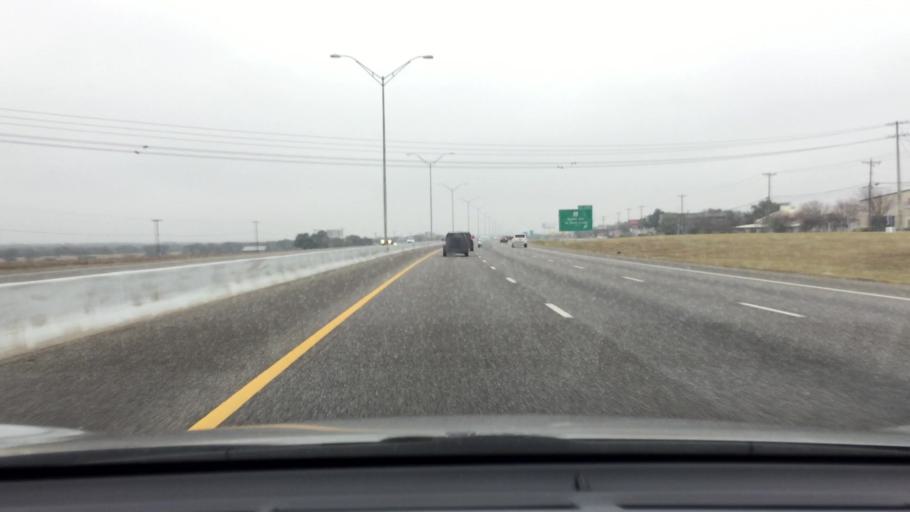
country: US
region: Texas
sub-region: Williamson County
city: Georgetown
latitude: 30.5938
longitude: -97.6907
